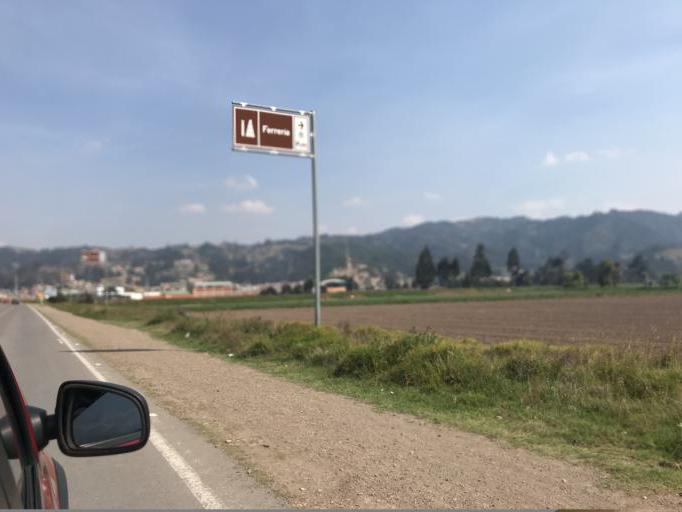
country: CO
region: Boyaca
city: Samaca
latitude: 5.5001
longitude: -73.4922
